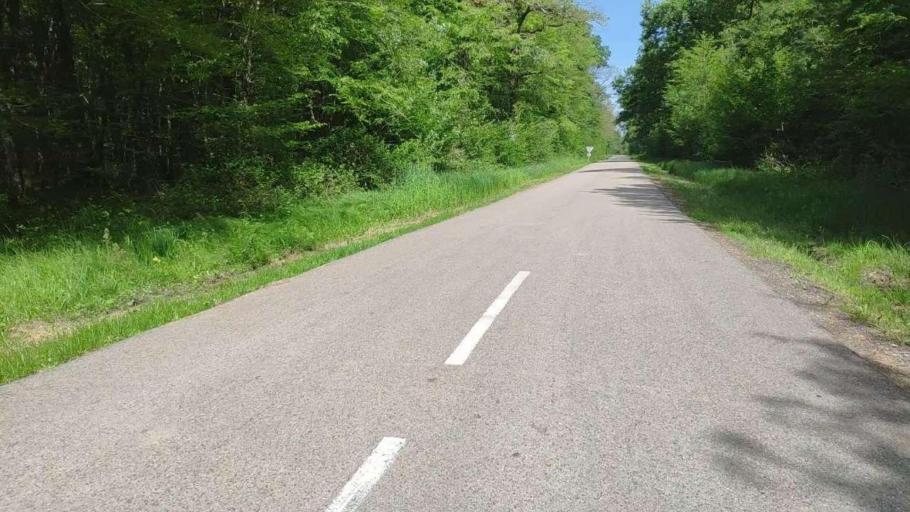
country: FR
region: Franche-Comte
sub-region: Departement du Jura
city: Bletterans
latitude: 46.7118
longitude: 5.3997
